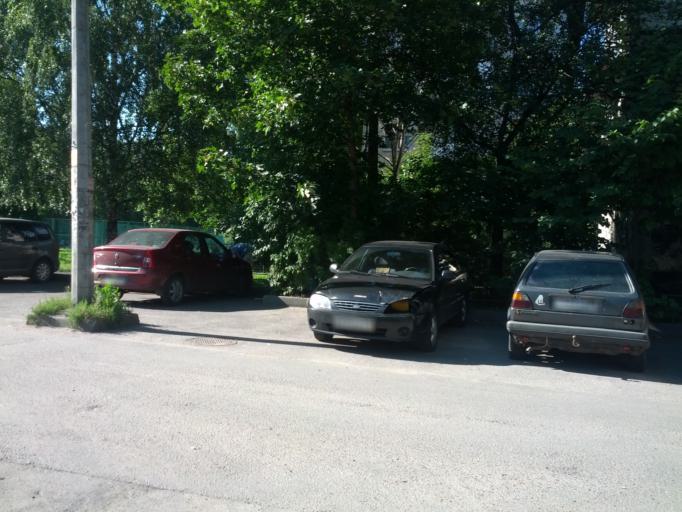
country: RU
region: Leningrad
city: Rybatskoye
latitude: 59.8972
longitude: 30.4868
